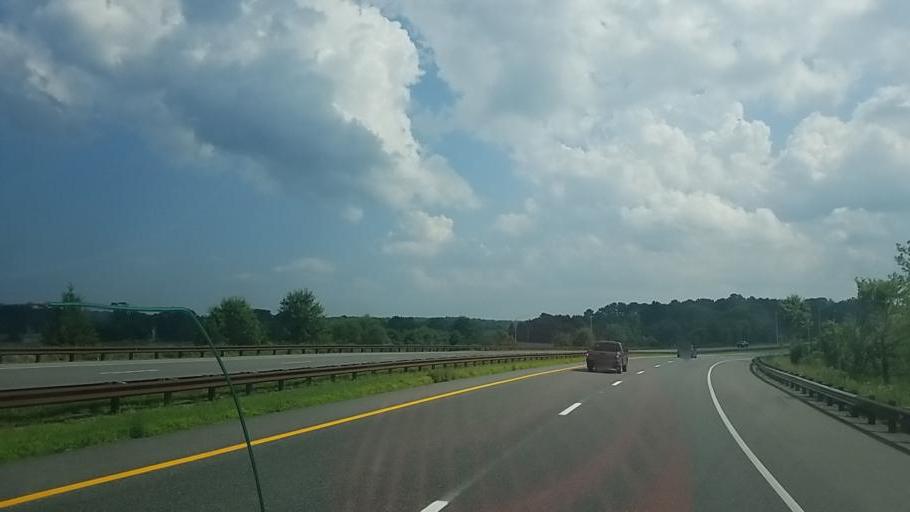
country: US
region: Maryland
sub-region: Worcester County
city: Ocean Pines
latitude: 38.3890
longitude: -75.2034
